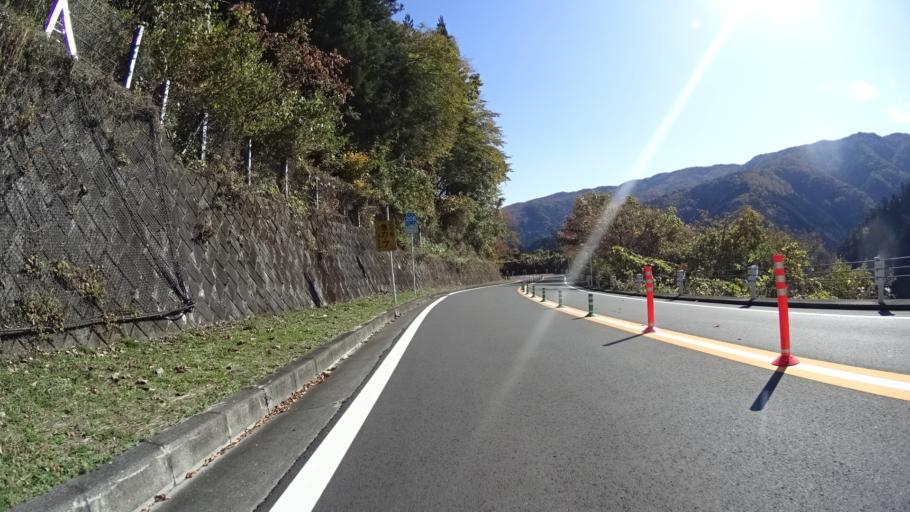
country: JP
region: Yamanashi
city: Uenohara
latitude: 35.7318
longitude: 139.0423
